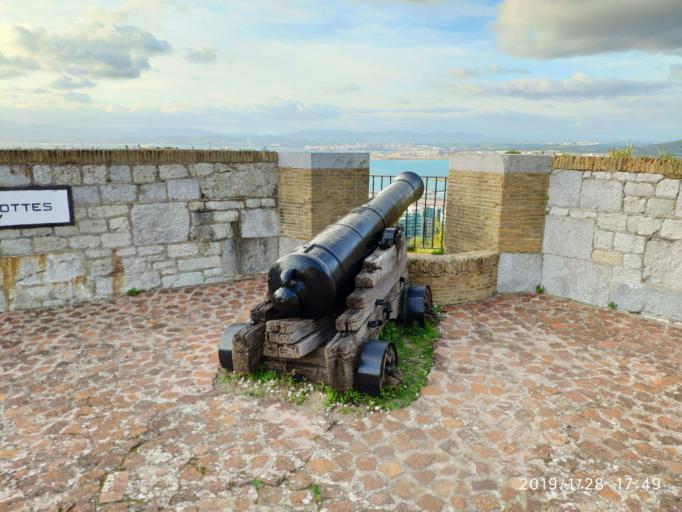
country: GI
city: Gibraltar
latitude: 36.1441
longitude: -5.3495
